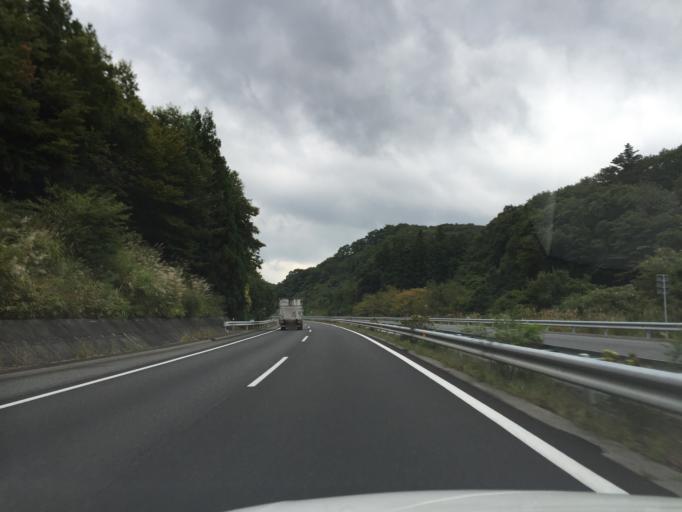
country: JP
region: Fukushima
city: Iwaki
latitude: 37.2035
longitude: 140.6954
